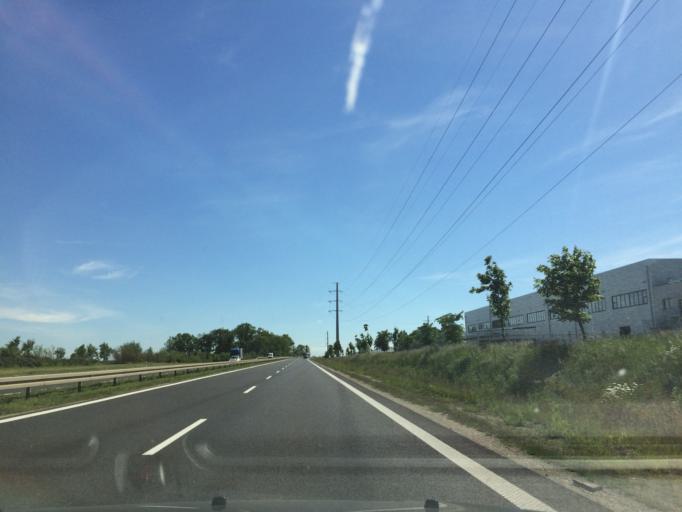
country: PL
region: Lower Silesian Voivodeship
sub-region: Powiat wroclawski
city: Tyniec Maly
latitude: 51.0195
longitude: 16.9046
